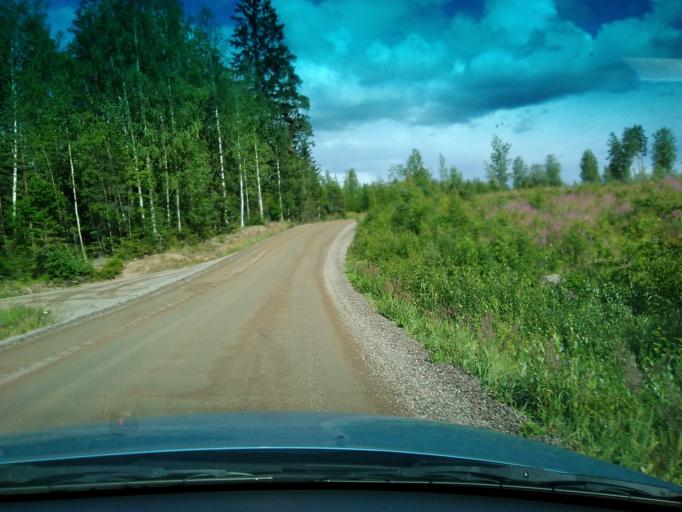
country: FI
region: Central Finland
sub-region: Saarijaervi-Viitasaari
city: Saarijaervi
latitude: 62.7322
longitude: 25.1049
